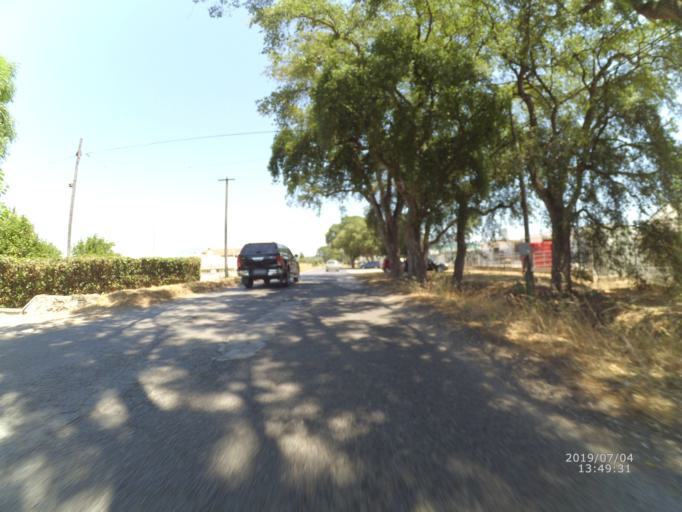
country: IT
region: Latium
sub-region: Provincia di Latina
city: San Felice Circeo
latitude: 41.2853
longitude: 13.1143
